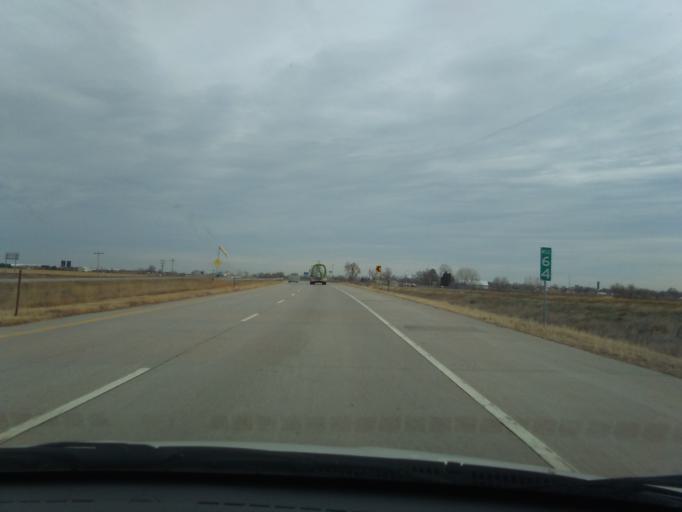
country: US
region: Colorado
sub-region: Morgan County
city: Fort Morgan
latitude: 40.2325
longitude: -104.0915
